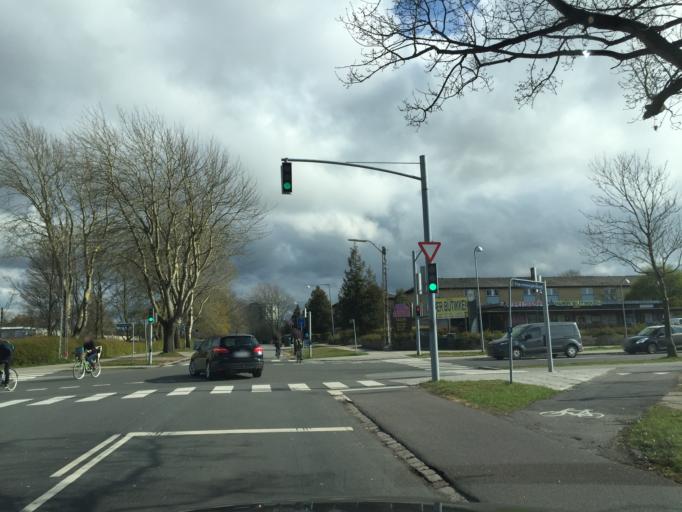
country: DK
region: South Denmark
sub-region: Odense Kommune
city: Neder Holluf
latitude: 55.3794
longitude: 10.4226
